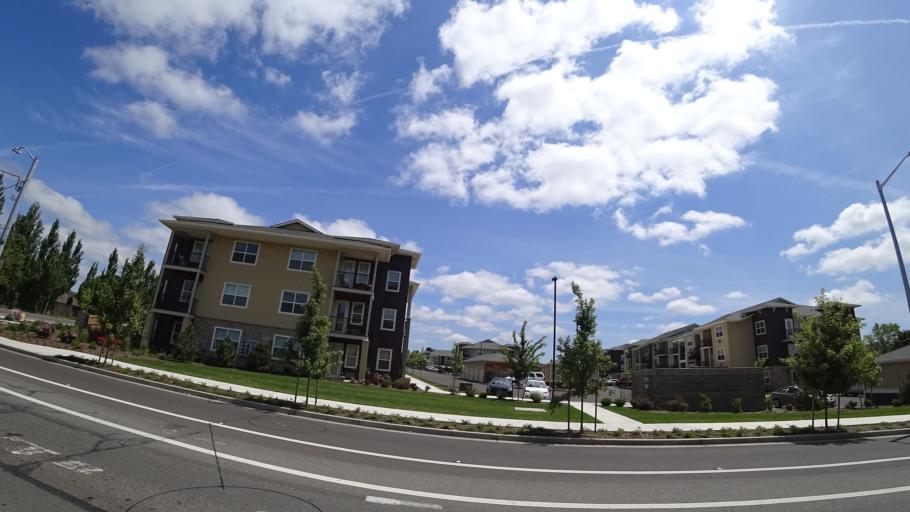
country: US
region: Oregon
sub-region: Washington County
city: King City
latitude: 45.4412
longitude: -122.8157
